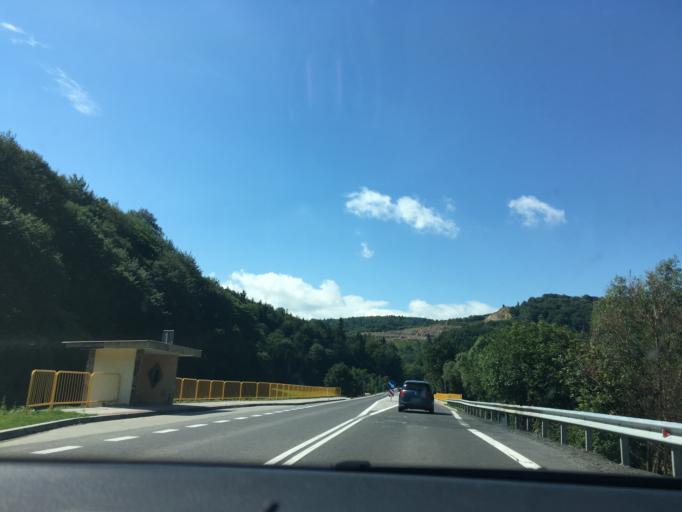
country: PL
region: Subcarpathian Voivodeship
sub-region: Powiat krosnienski
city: Dukla
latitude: 49.5214
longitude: 21.6898
